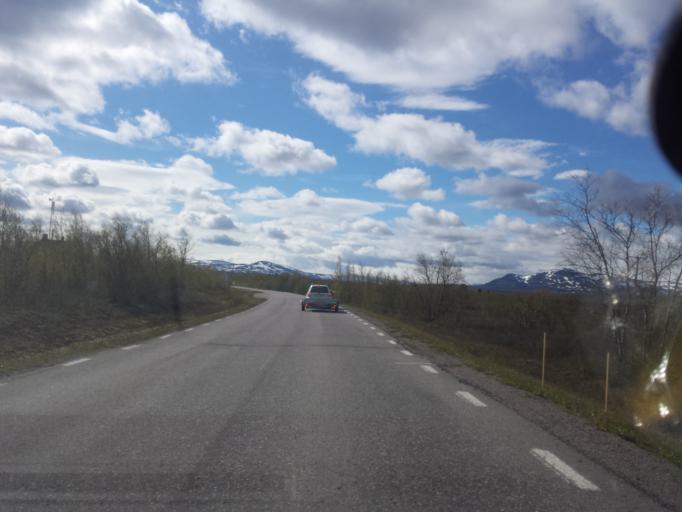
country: SE
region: Norrbotten
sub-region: Kiruna Kommun
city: Kiruna
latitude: 67.9948
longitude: 19.8996
